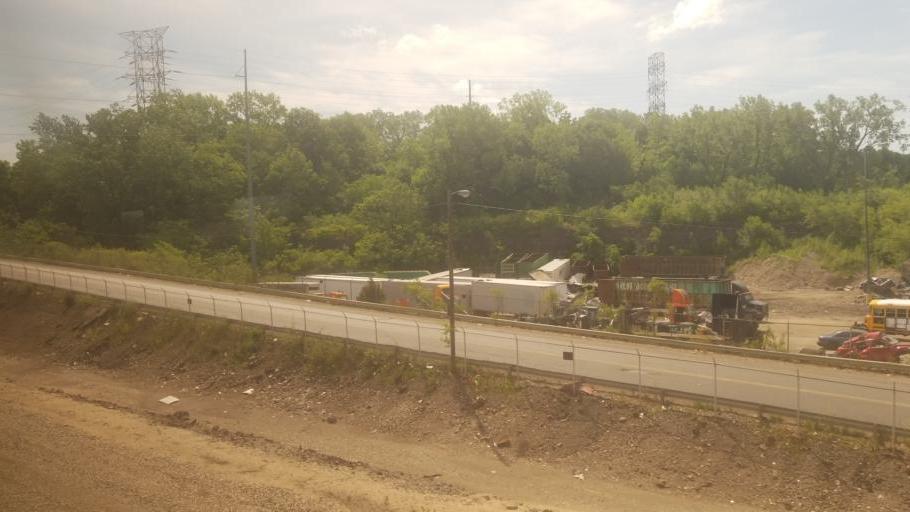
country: US
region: Missouri
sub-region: Jackson County
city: Sugar Creek
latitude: 39.1123
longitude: -94.4898
